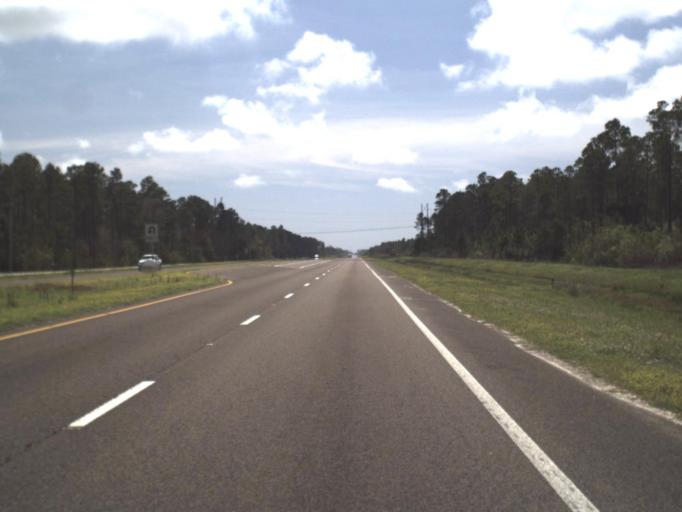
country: US
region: Florida
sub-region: Bay County
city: Laguna Beach
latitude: 30.2856
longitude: -85.8640
